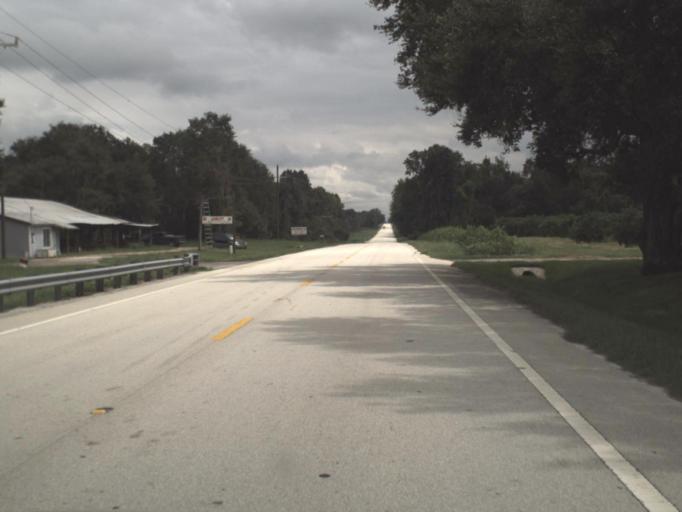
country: US
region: Florida
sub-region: Hardee County
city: Bowling Green
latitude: 27.5948
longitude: -81.9306
